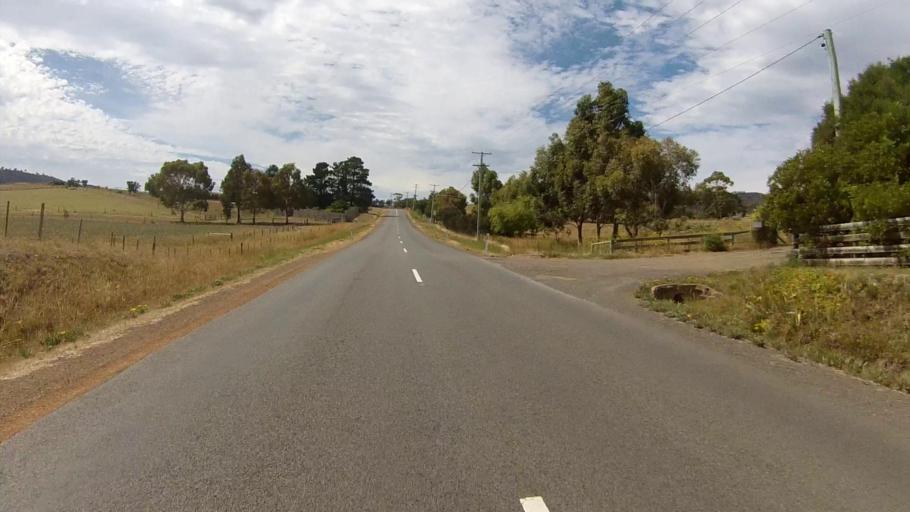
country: AU
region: Tasmania
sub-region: Brighton
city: Old Beach
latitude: -42.6940
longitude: 147.3473
